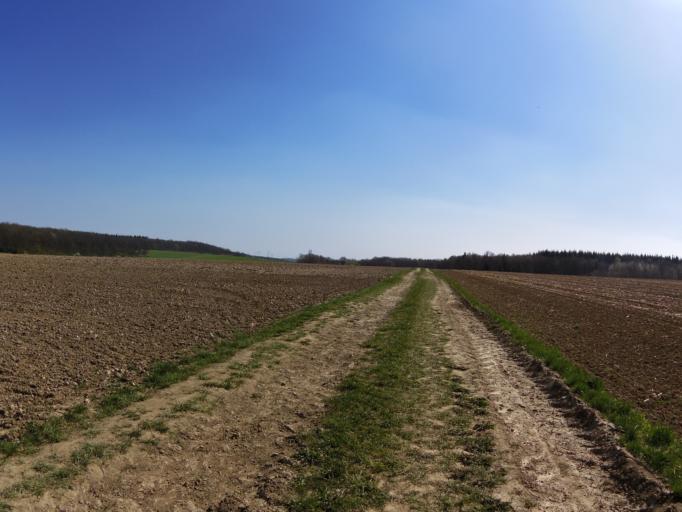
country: DE
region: Bavaria
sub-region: Regierungsbezirk Unterfranken
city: Kurnach
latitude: 49.8339
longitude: 10.0458
